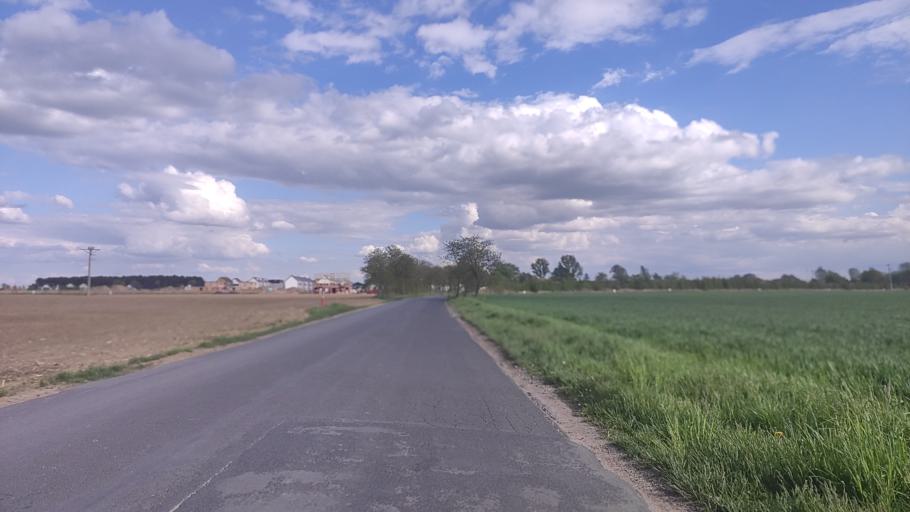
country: PL
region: Greater Poland Voivodeship
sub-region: Powiat poznanski
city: Swarzedz
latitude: 52.3938
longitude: 17.1153
